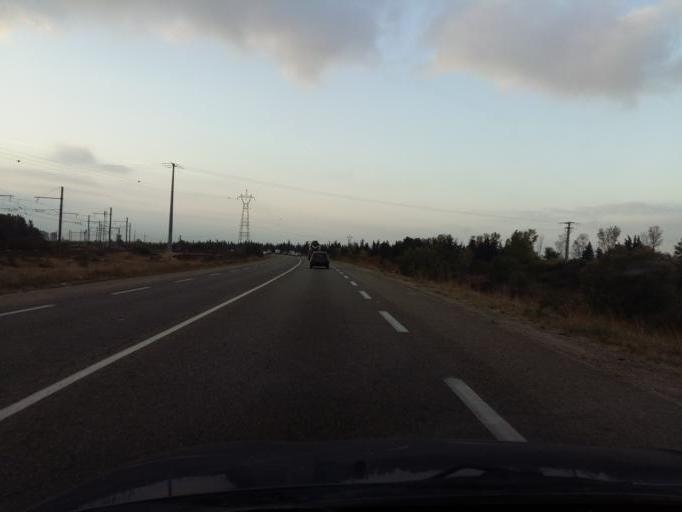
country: FR
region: Provence-Alpes-Cote d'Azur
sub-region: Departement des Bouches-du-Rhone
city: Istres
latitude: 43.5478
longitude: 4.9561
